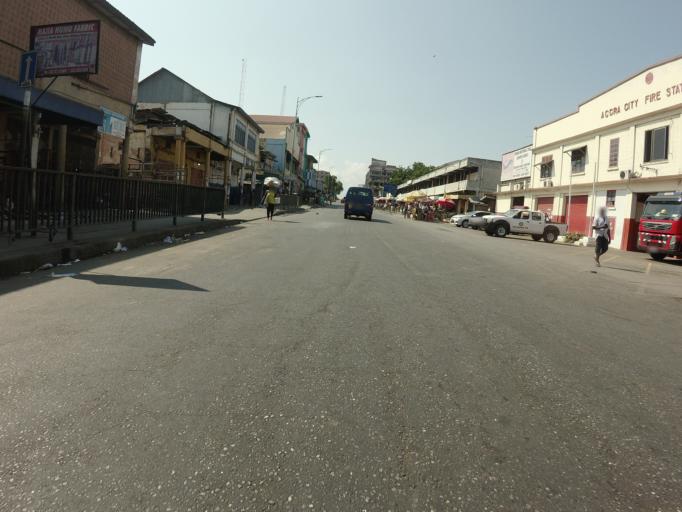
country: GH
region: Greater Accra
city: Accra
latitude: 5.5491
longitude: -0.2074
